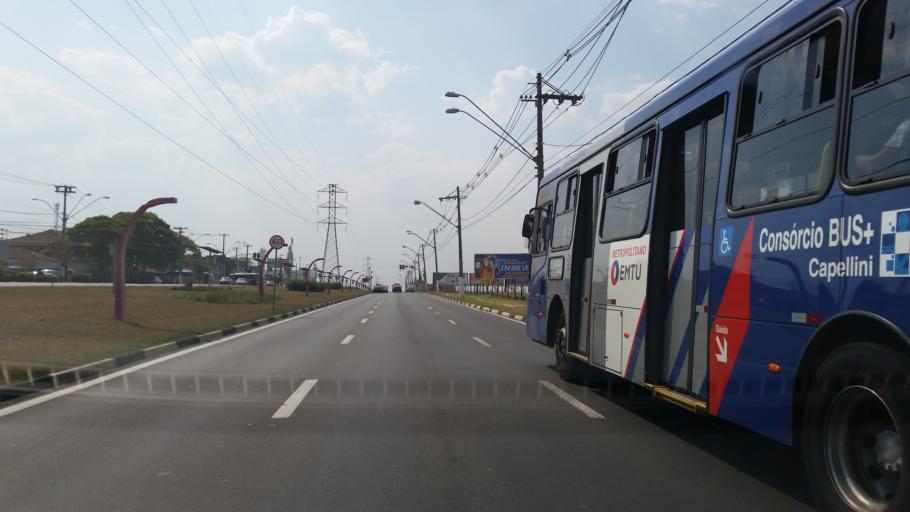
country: BR
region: Sao Paulo
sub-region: Hortolandia
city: Hortolandia
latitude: -22.8905
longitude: -47.1913
